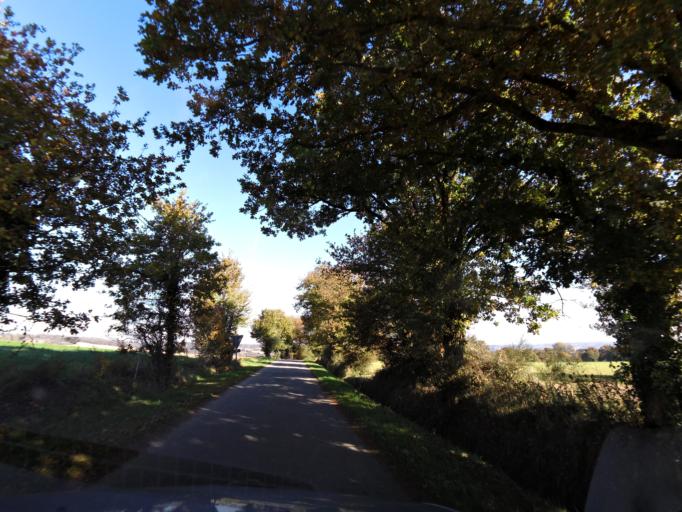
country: FR
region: Brittany
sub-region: Departement d'Ille-et-Vilaine
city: Bain-de-Bretagne
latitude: 47.8494
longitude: -1.7074
